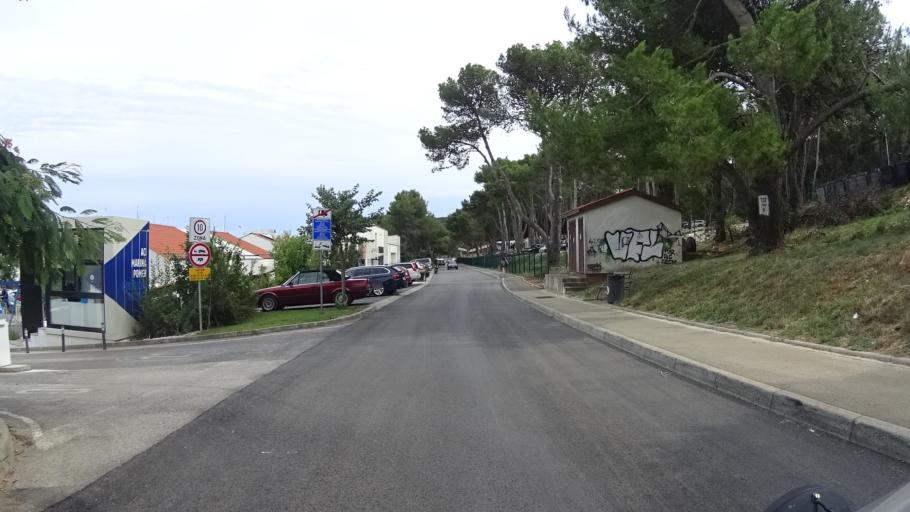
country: HR
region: Istarska
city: Medulin
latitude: 44.8220
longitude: 13.9008
